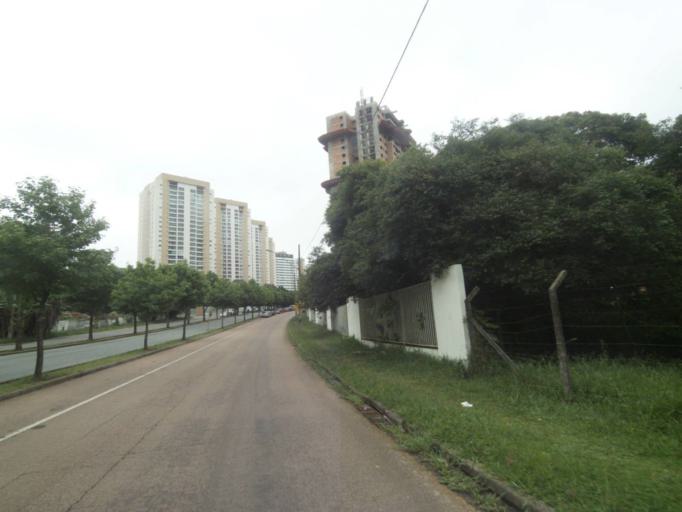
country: BR
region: Parana
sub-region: Curitiba
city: Curitiba
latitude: -25.4420
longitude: -49.3504
